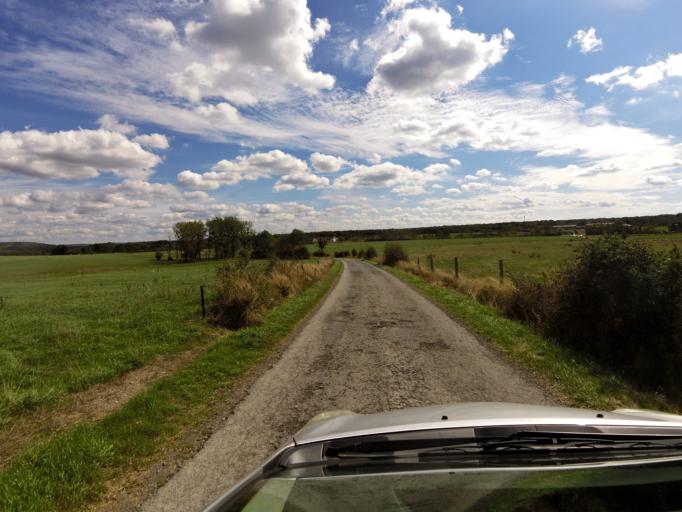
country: BE
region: Wallonia
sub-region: Province du Luxembourg
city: Durbuy
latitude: 50.3275
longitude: 5.4183
